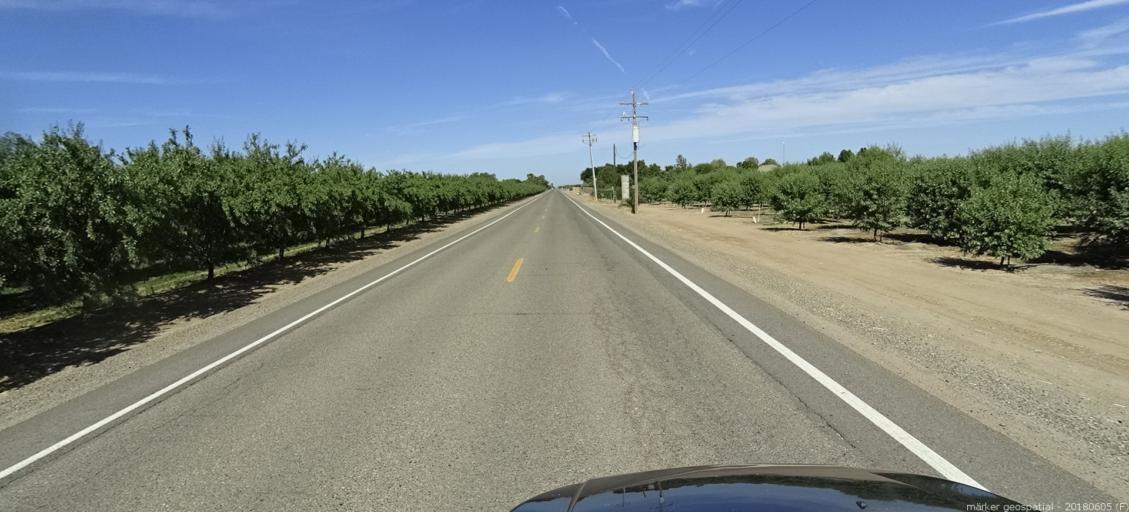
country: US
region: California
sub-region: Madera County
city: Chowchilla
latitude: 37.1127
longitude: -120.3552
